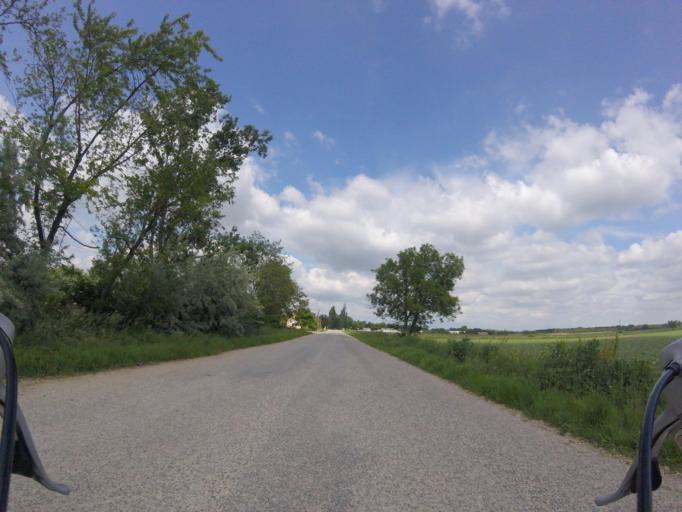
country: HU
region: Fejer
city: Szabadbattyan
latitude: 47.0876
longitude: 18.4156
